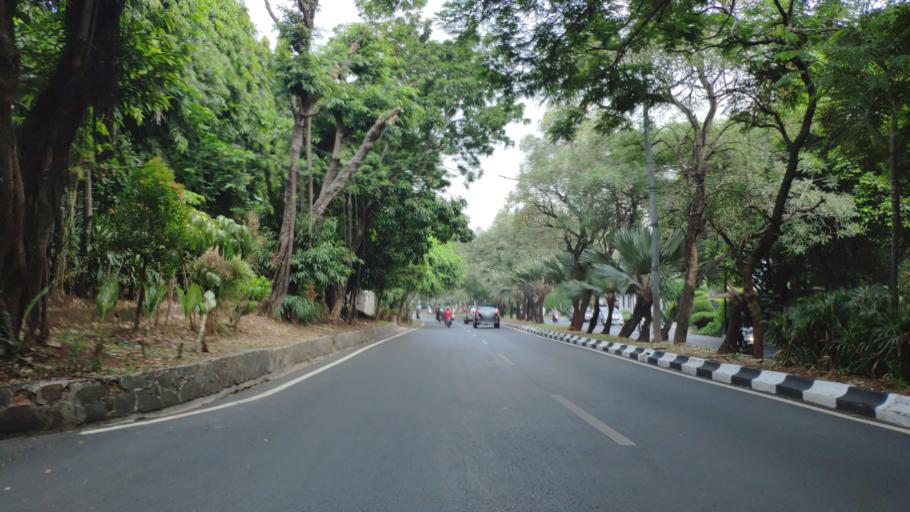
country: ID
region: Banten
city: South Tangerang
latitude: -6.2825
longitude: 106.7855
